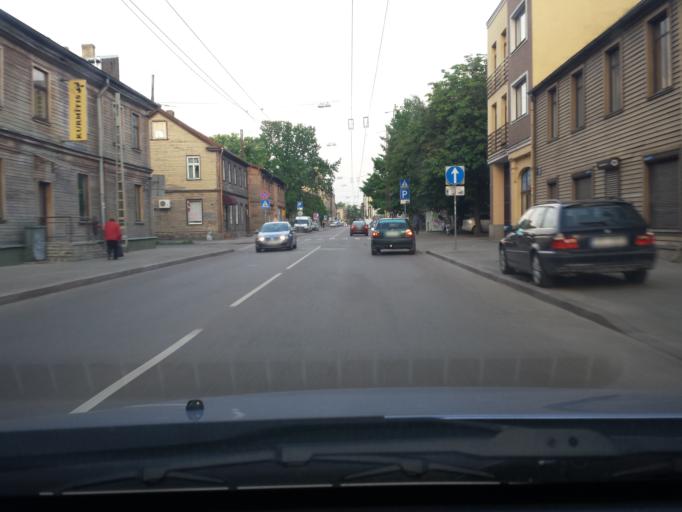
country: LV
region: Riga
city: Riga
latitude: 56.9586
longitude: 24.1445
